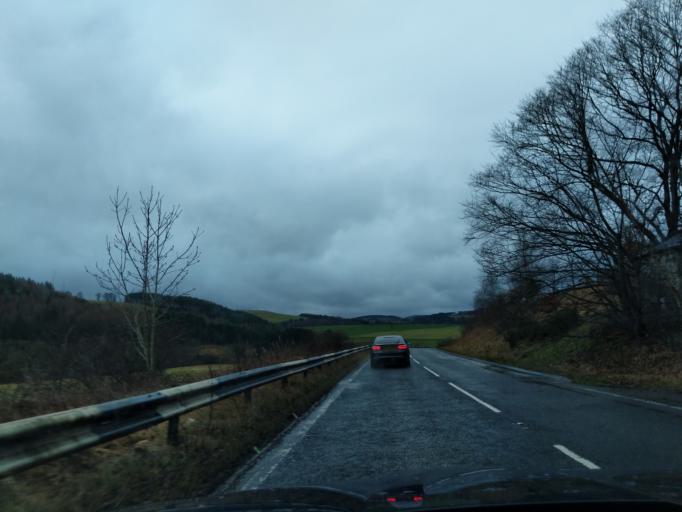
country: GB
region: Scotland
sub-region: The Scottish Borders
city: Galashiels
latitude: 55.6416
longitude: -2.8425
